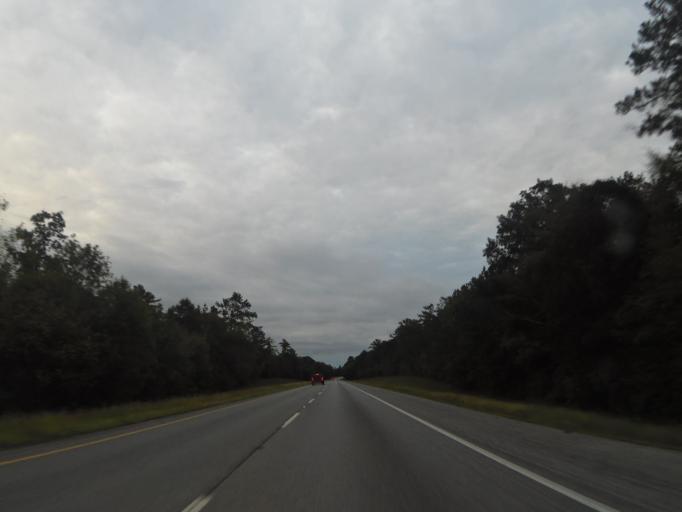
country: US
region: Alabama
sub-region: Saint Clair County
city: Steele
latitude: 33.9083
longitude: -86.2225
